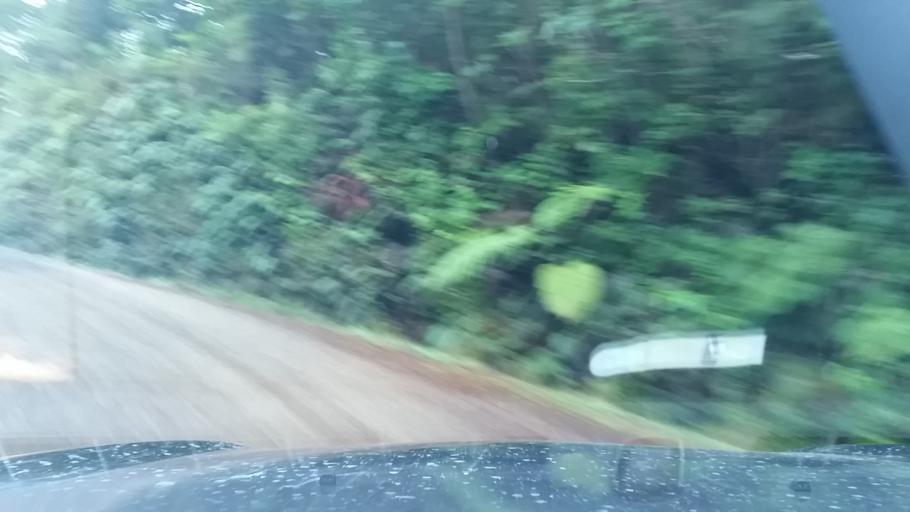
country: NZ
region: Marlborough
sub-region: Marlborough District
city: Picton
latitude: -41.1168
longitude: 173.9932
